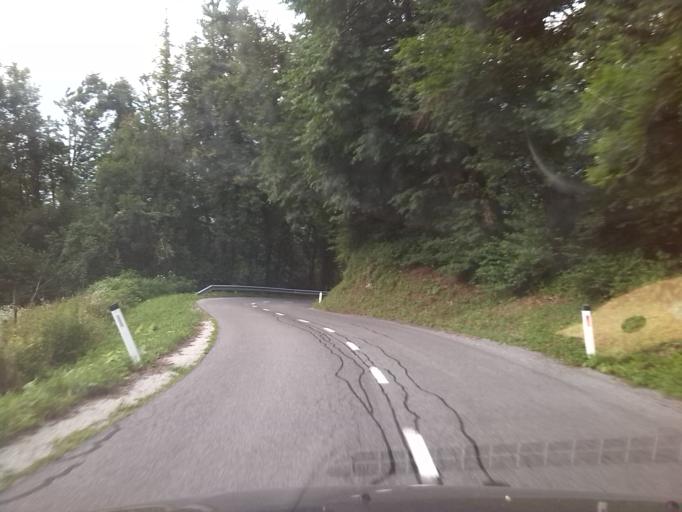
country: SI
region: Kobarid
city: Kobarid
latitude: 46.2139
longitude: 13.5941
